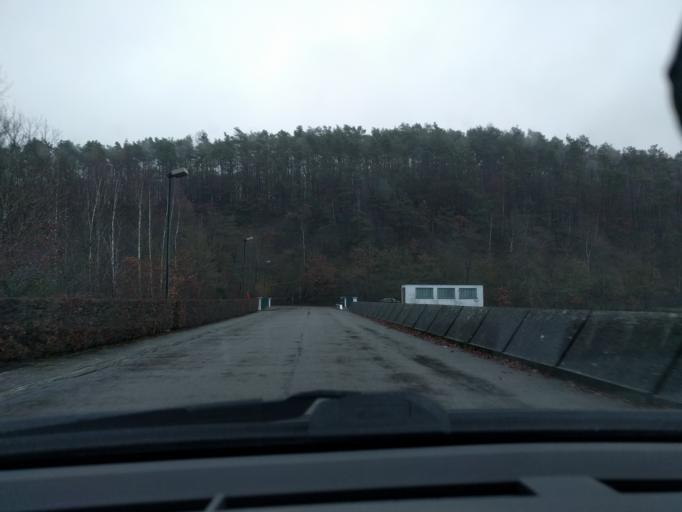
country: BE
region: Wallonia
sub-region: Province de Namur
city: Couvin
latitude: 50.0238
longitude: 4.5361
